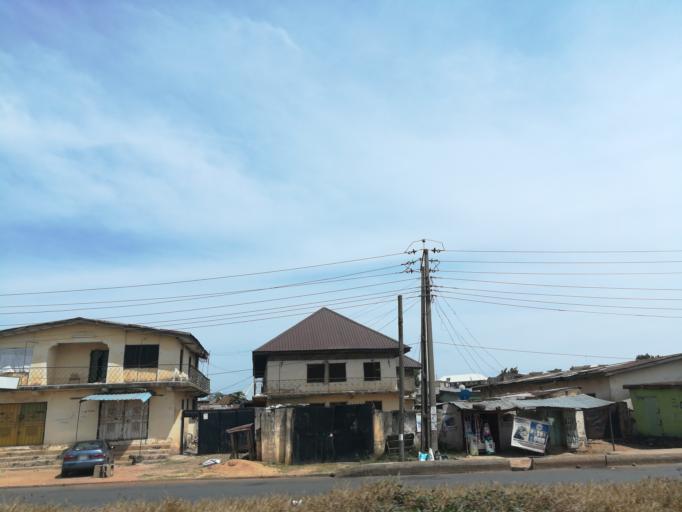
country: NG
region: Plateau
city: Bukuru
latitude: 9.7992
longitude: 8.8593
